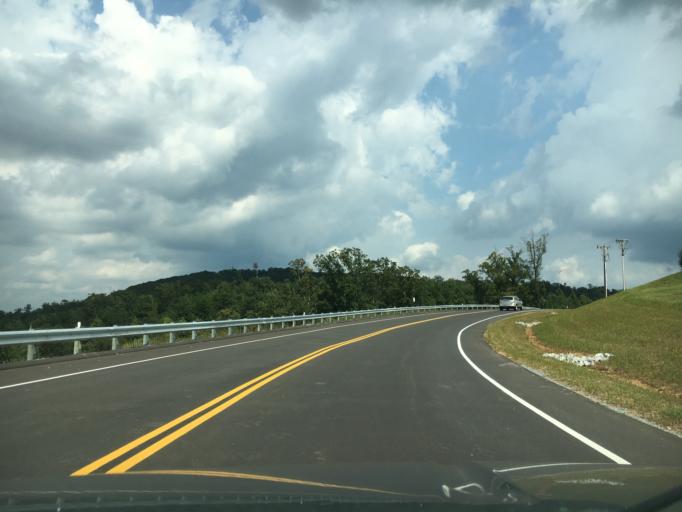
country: US
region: Virginia
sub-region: City of Lynchburg
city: West Lynchburg
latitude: 37.3375
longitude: -79.1806
